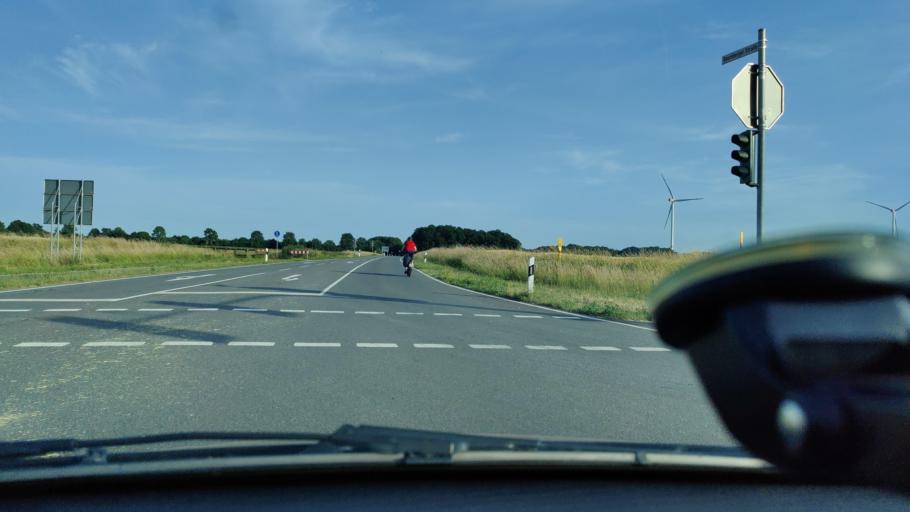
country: DE
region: North Rhine-Westphalia
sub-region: Regierungsbezirk Munster
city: Billerbeck
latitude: 52.0143
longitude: 7.2163
